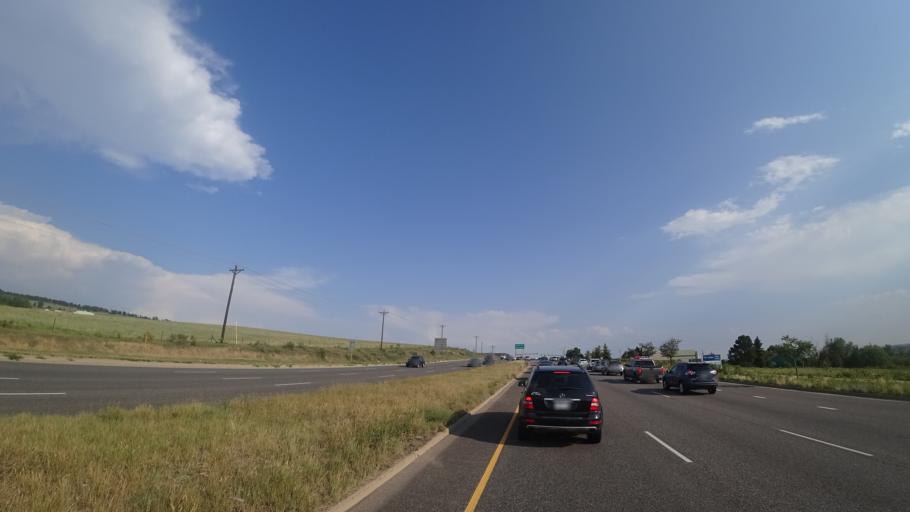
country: US
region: Colorado
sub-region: Douglas County
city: Parker
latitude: 39.5469
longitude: -104.7734
